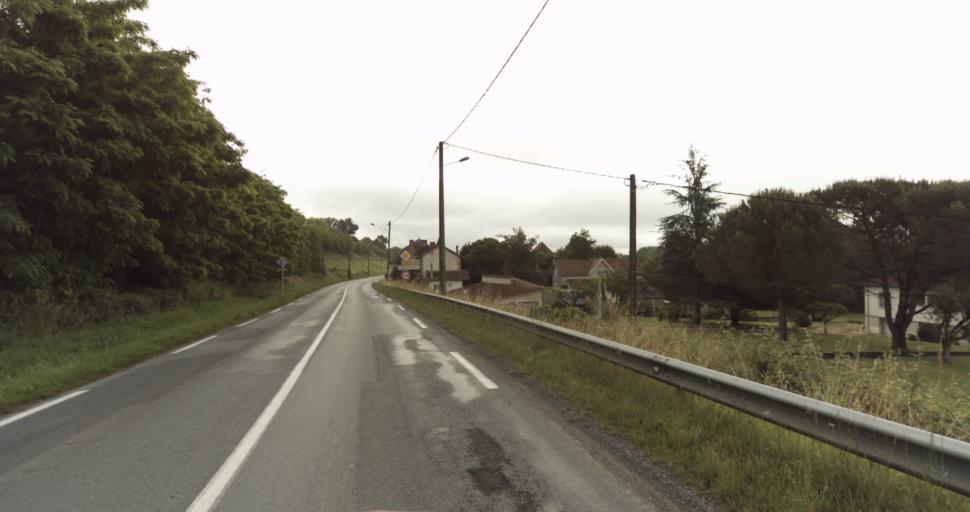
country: FR
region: Aquitaine
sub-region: Departement de la Dordogne
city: Mouleydier
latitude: 44.8552
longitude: 0.5836
